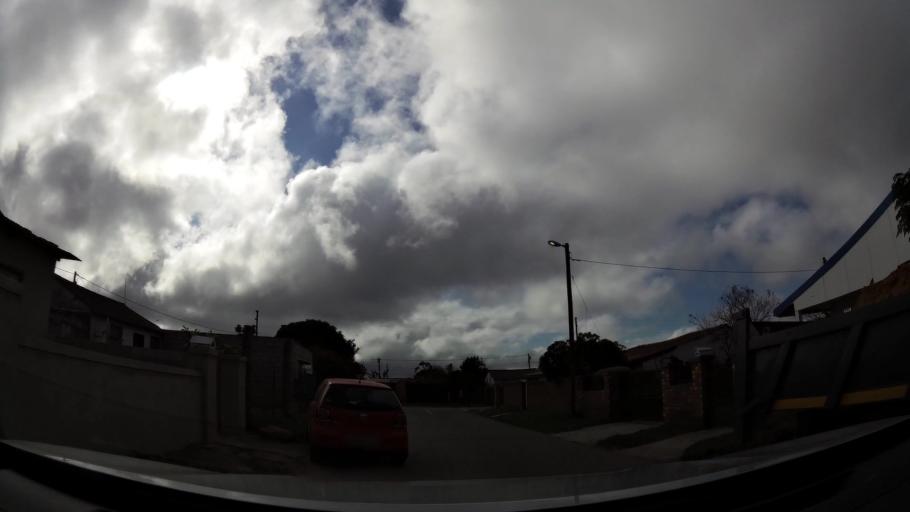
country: ZA
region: Western Cape
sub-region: Eden District Municipality
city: Plettenberg Bay
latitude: -34.0483
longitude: 23.3247
